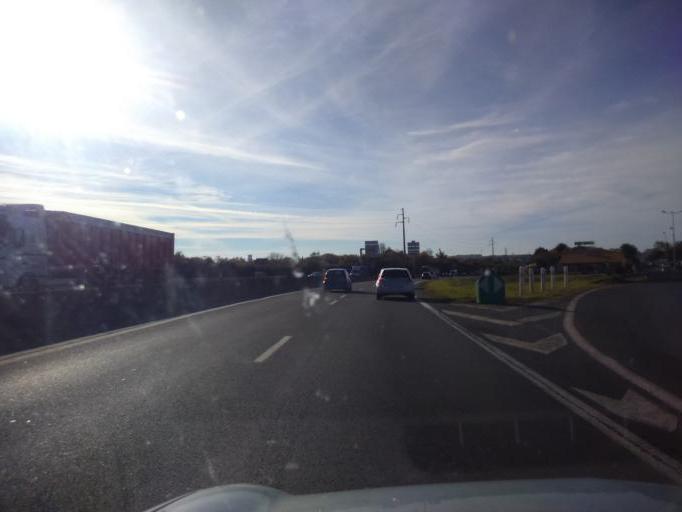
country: FR
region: Poitou-Charentes
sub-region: Departement de la Charente-Maritime
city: Puilboreau
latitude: 46.1712
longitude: -1.1207
